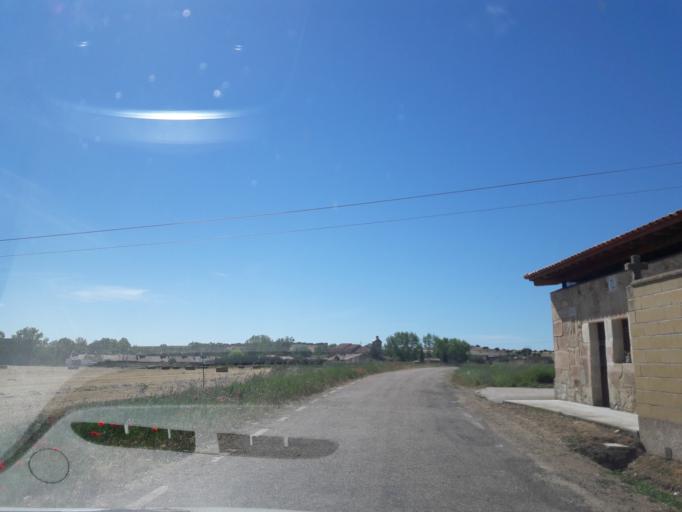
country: ES
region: Castille and Leon
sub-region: Provincia de Salamanca
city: Zarapicos
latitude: 41.0406
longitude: -5.8472
